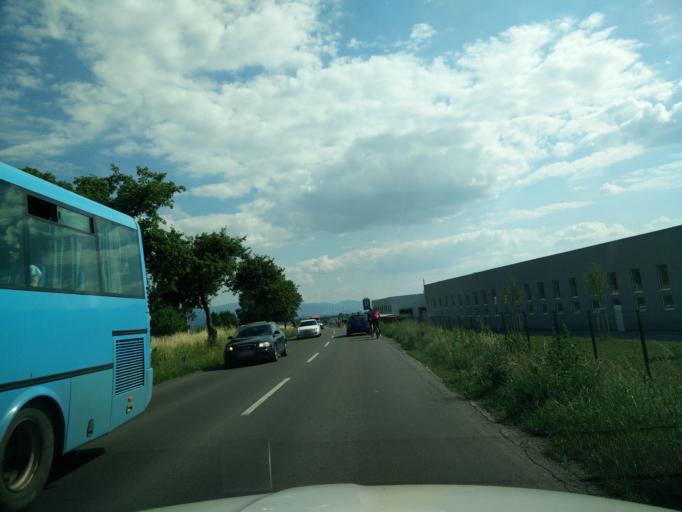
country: SK
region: Nitriansky
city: Prievidza
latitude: 48.8379
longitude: 18.6441
